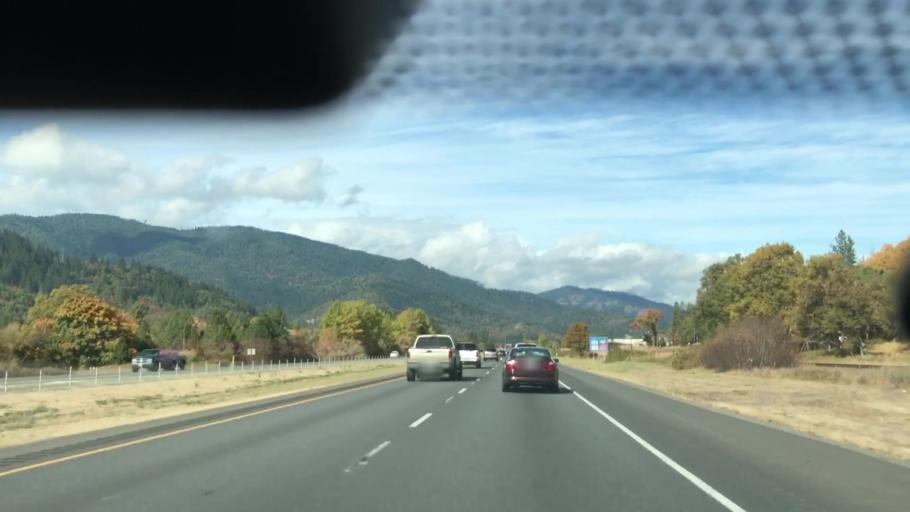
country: US
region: Oregon
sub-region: Jackson County
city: Rogue River
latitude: 42.4178
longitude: -123.1580
